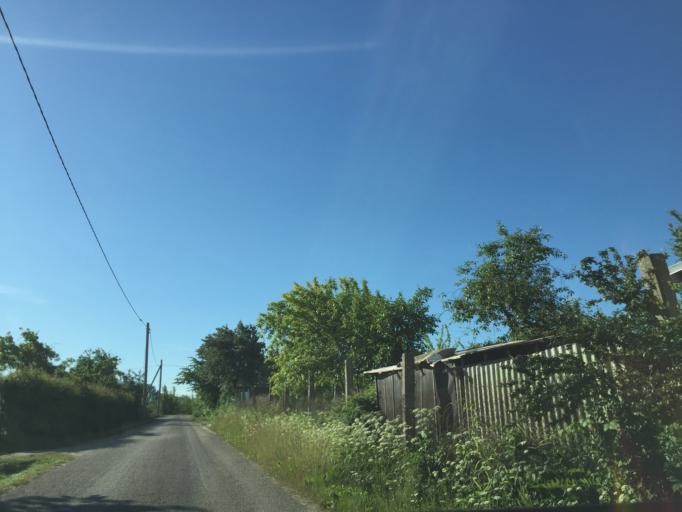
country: LV
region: Ventspils
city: Ventspils
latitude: 57.3697
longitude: 21.6076
